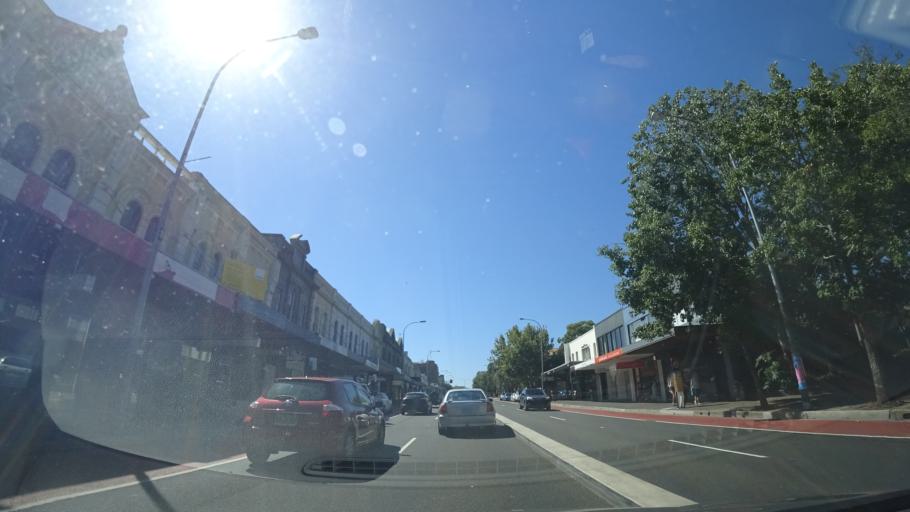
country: AU
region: New South Wales
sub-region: Woollahra
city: Paddington
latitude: -33.8875
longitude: 151.2308
